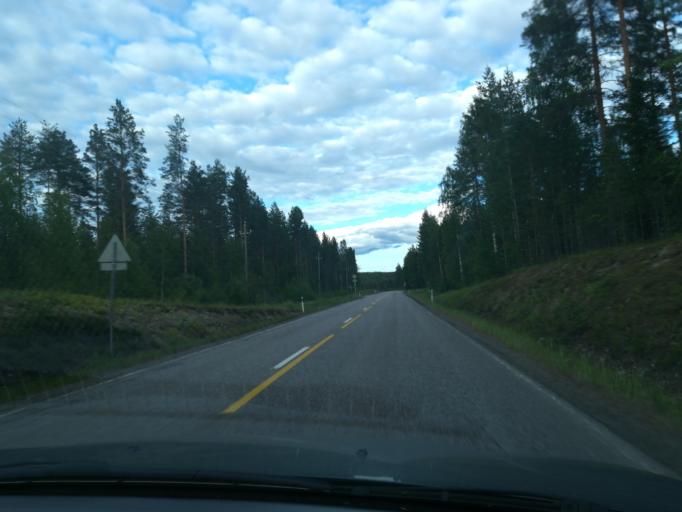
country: FI
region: Southern Savonia
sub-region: Mikkeli
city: Puumala
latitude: 61.5601
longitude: 28.0244
